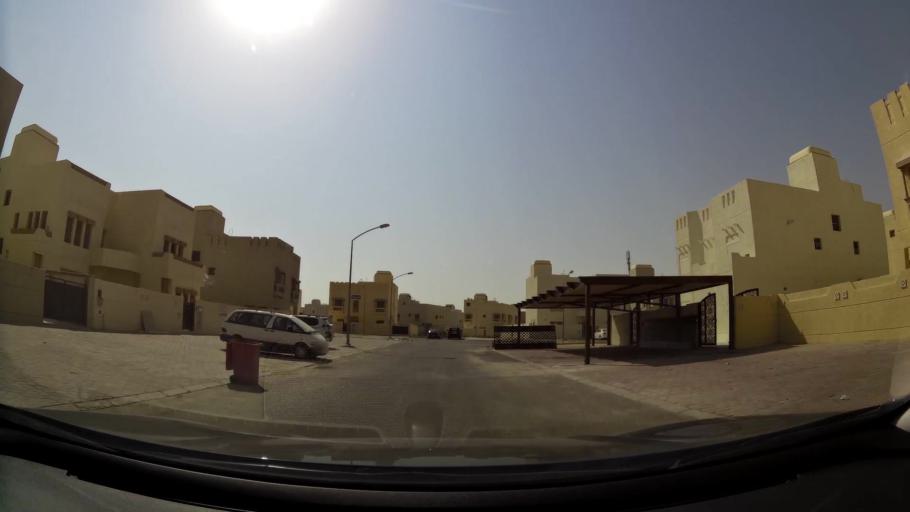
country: KW
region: Al Ahmadi
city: Al Wafrah
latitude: 28.8105
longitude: 48.0558
